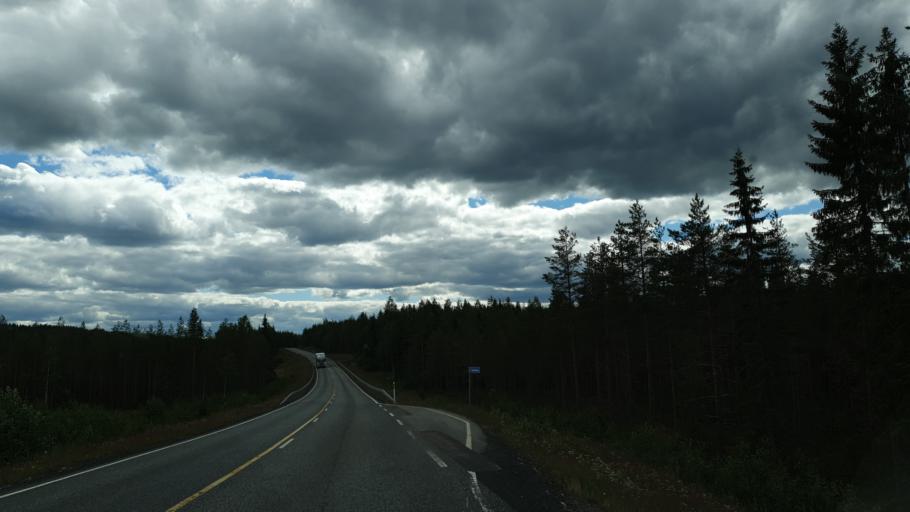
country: FI
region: Kainuu
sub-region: Kehys-Kainuu
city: Kuhmo
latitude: 64.0053
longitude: 29.6267
